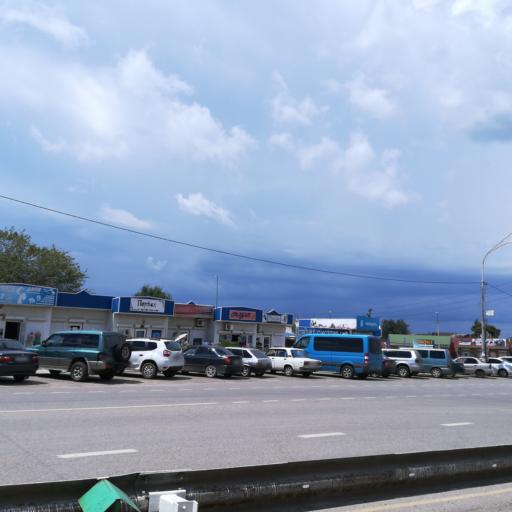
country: RU
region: Krasnodarskiy
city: Taman'
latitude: 45.2150
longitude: 36.7193
